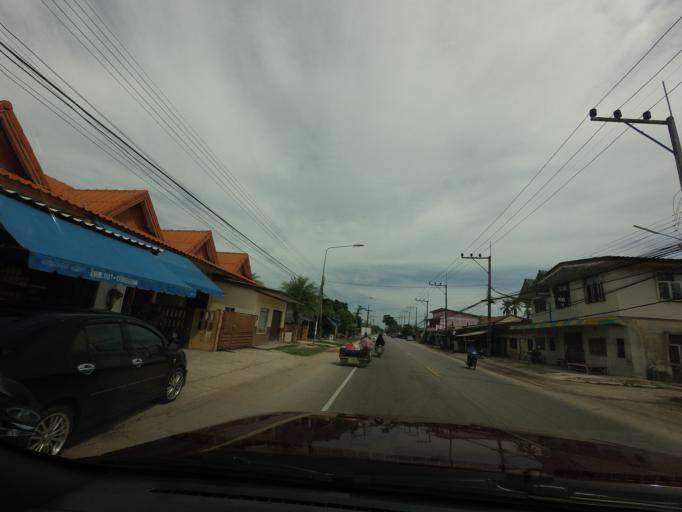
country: TH
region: Narathiwat
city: Tak Bai
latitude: 6.2516
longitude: 102.0650
